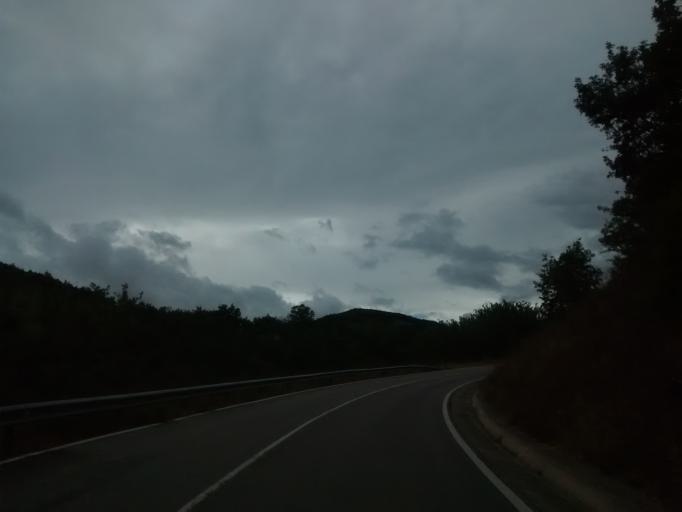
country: ES
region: Castille and Leon
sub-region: Provincia de Palencia
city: Berzosilla
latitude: 42.8592
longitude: -4.0434
